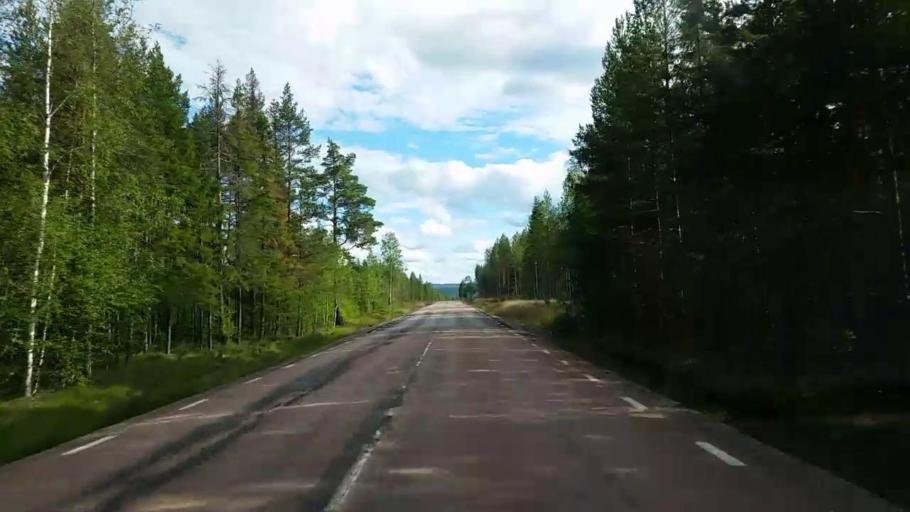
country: SE
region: Gaevleborg
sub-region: Ljusdals Kommun
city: Farila
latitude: 61.9508
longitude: 15.8849
